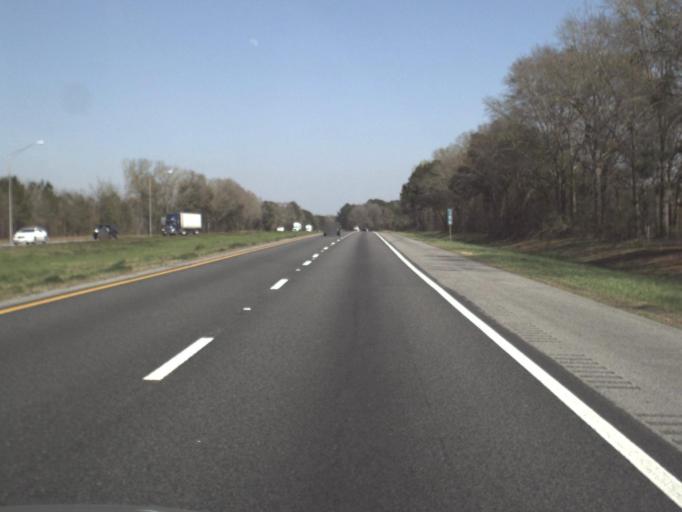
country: US
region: Florida
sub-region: Jackson County
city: Sneads
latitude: 30.6403
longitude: -84.9729
